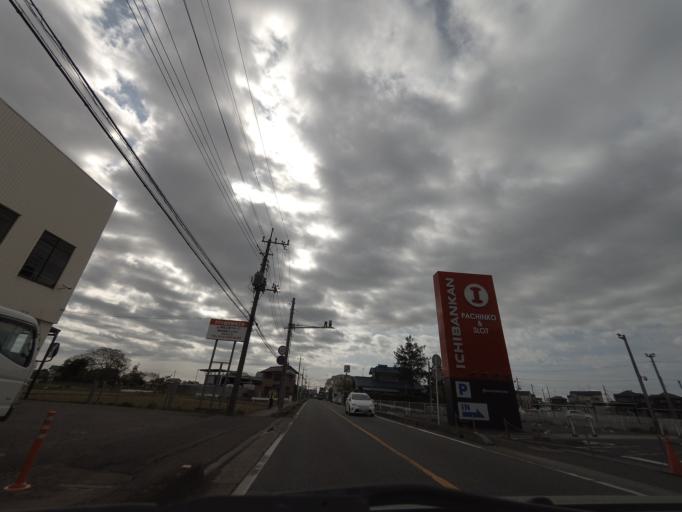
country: JP
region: Saitama
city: Kamifukuoka
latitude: 35.8840
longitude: 139.5447
